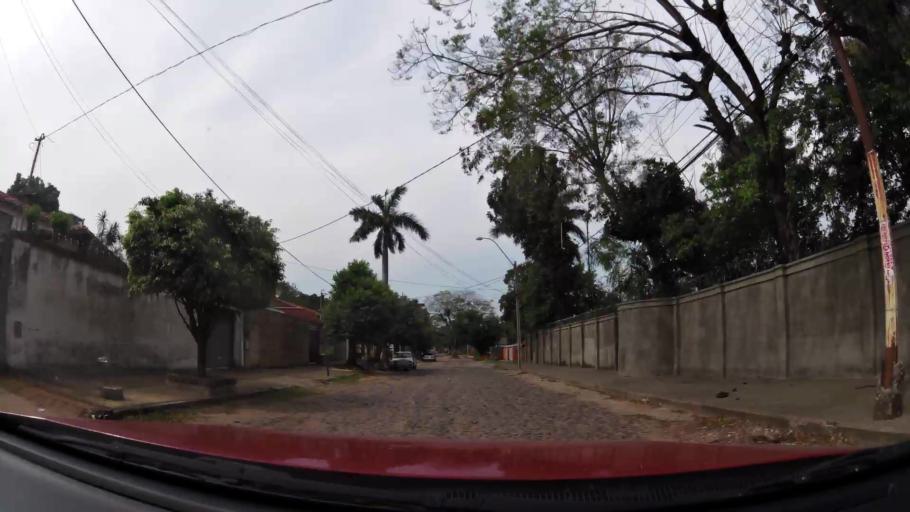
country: PY
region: Central
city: Fernando de la Mora
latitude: -25.2765
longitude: -57.5566
